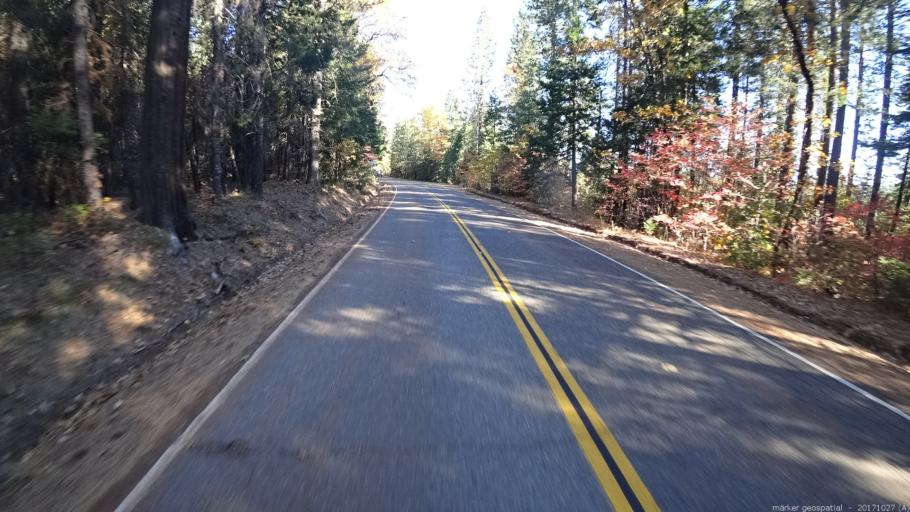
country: US
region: California
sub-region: Shasta County
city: Burney
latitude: 40.9702
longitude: -121.9296
